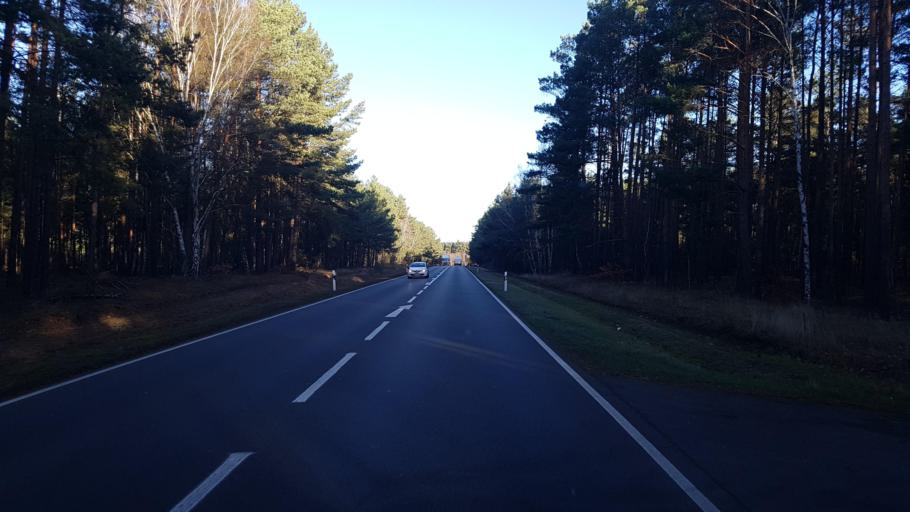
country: DE
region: Brandenburg
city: Heinersbruck
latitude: 51.7240
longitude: 14.4586
